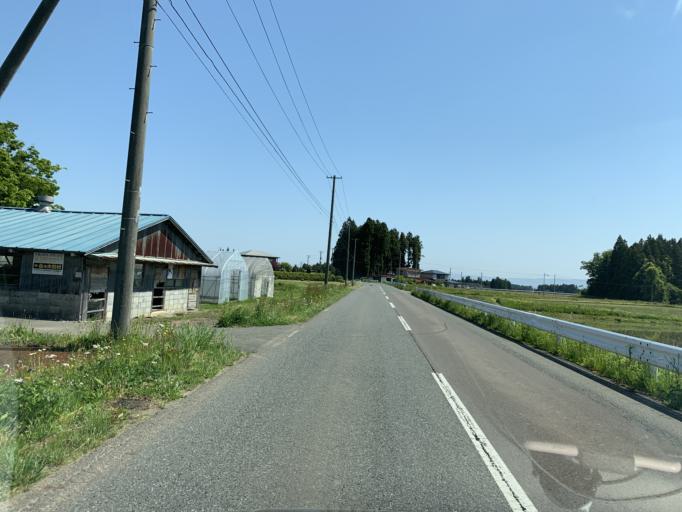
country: JP
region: Iwate
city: Mizusawa
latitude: 39.0790
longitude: 141.0640
